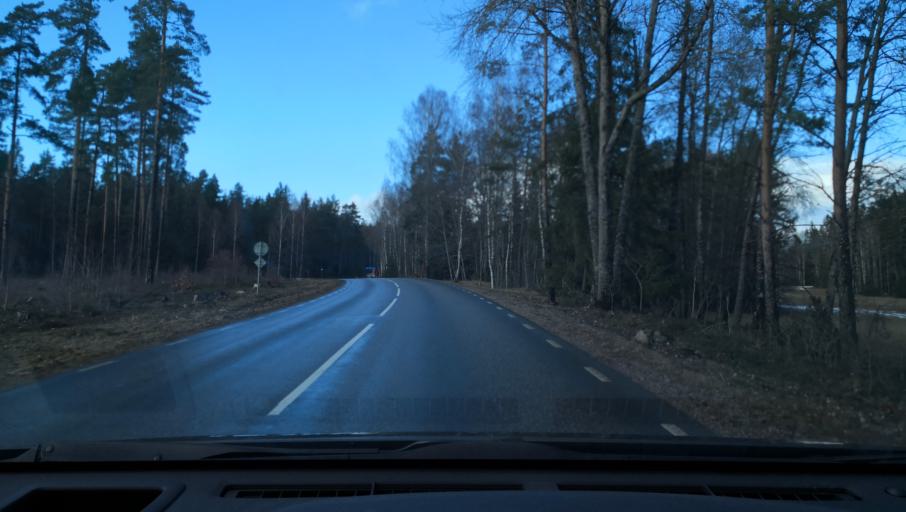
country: SE
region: Vaestmanland
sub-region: Arboga Kommun
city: Arboga
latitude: 59.3610
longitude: 15.8484
